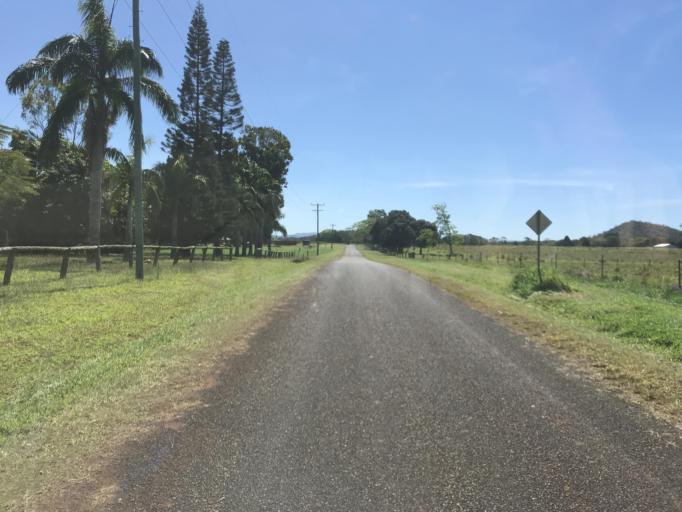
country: AU
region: Queensland
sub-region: Tablelands
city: Atherton
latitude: -17.2795
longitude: 145.5442
